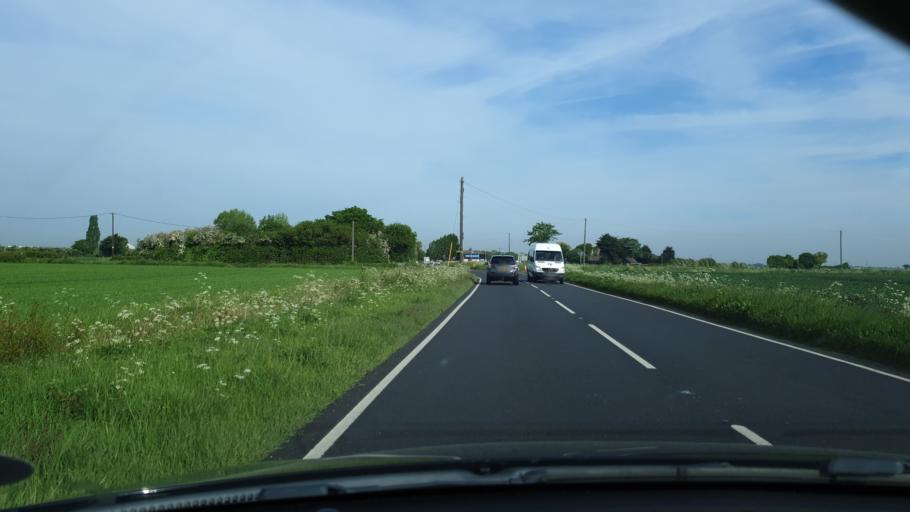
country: GB
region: England
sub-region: Essex
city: Little Clacton
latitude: 51.8492
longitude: 1.1906
